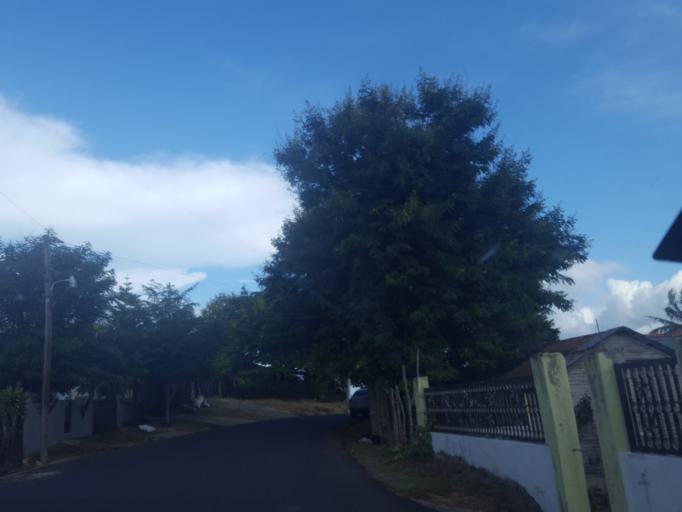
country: DO
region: La Vega
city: Rio Verde Arriba
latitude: 19.3507
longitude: -70.6269
